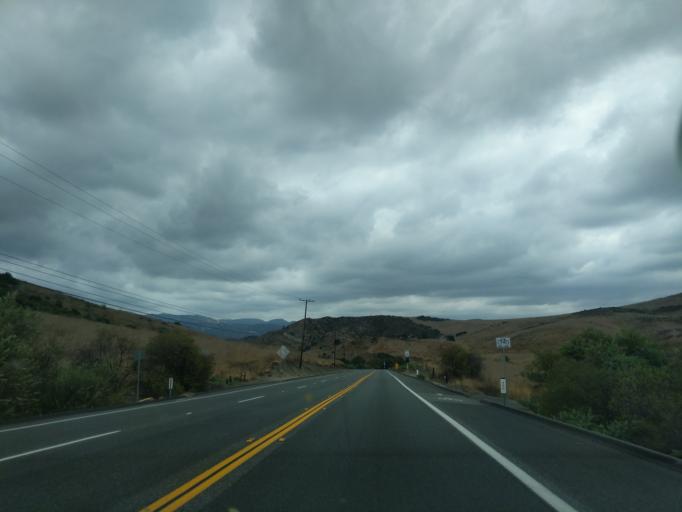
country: US
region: California
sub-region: Orange County
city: North Tustin
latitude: 33.7686
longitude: -117.7334
